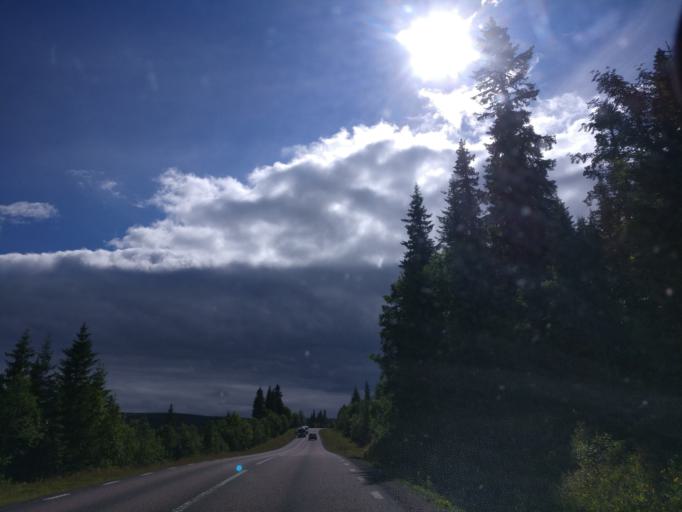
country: SE
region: Dalarna
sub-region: Malung-Saelens kommun
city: Malung
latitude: 61.1637
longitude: 13.1456
